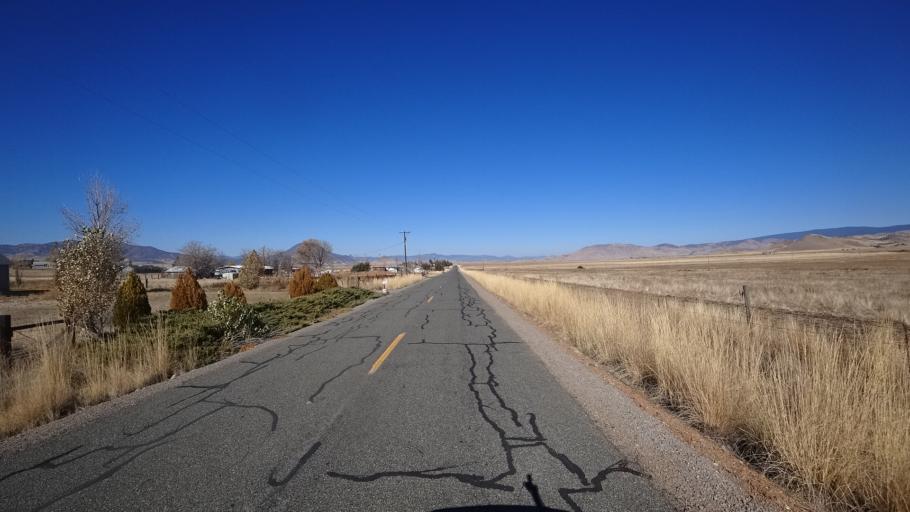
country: US
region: California
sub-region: Siskiyou County
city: Montague
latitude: 41.7571
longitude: -122.4571
